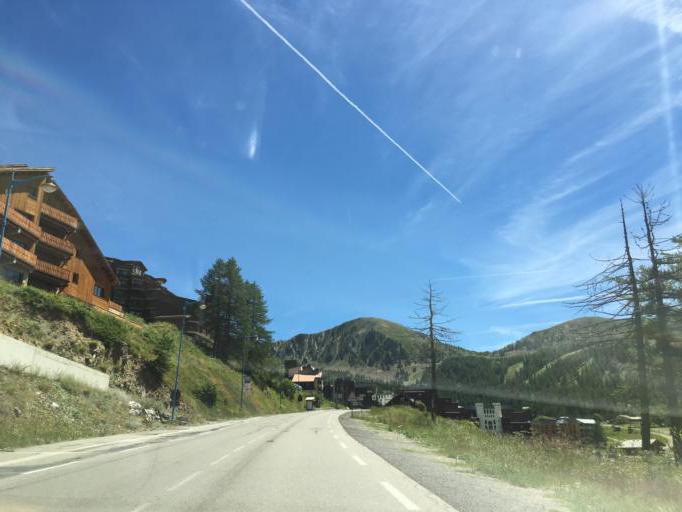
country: IT
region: Piedmont
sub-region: Provincia di Cuneo
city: Vinadio
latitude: 44.1881
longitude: 7.1561
